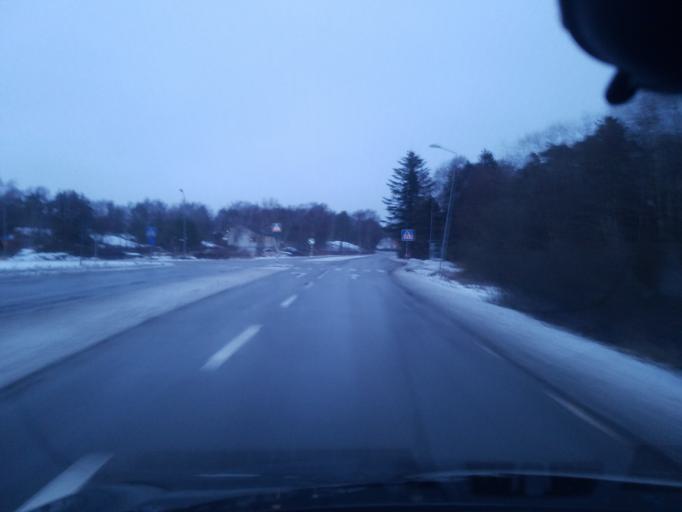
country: SE
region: Vaestra Goetaland
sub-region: Lysekils Kommun
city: Lysekil
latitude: 58.2868
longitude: 11.4732
